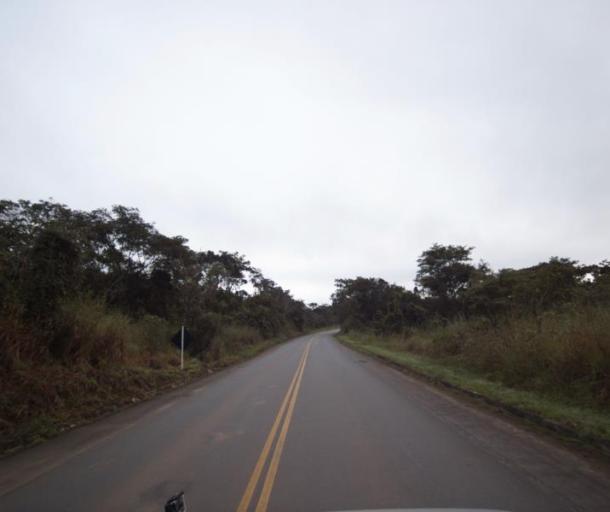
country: BR
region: Goias
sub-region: Pirenopolis
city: Pirenopolis
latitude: -15.8650
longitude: -48.7731
